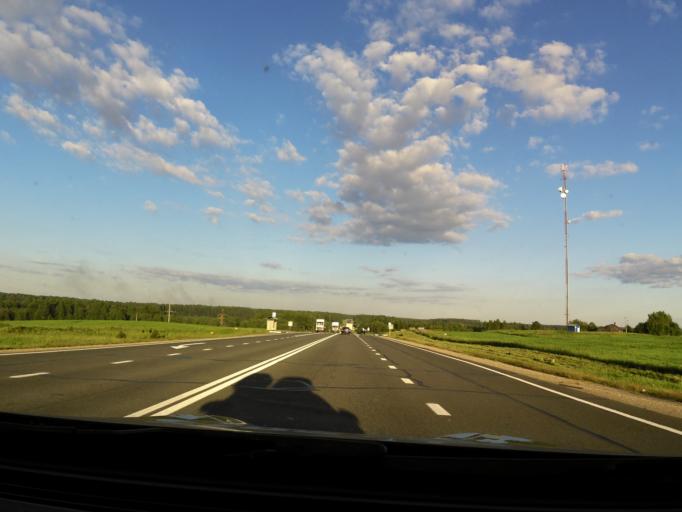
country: RU
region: Vologda
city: Vologda
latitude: 59.0595
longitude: 40.0605
